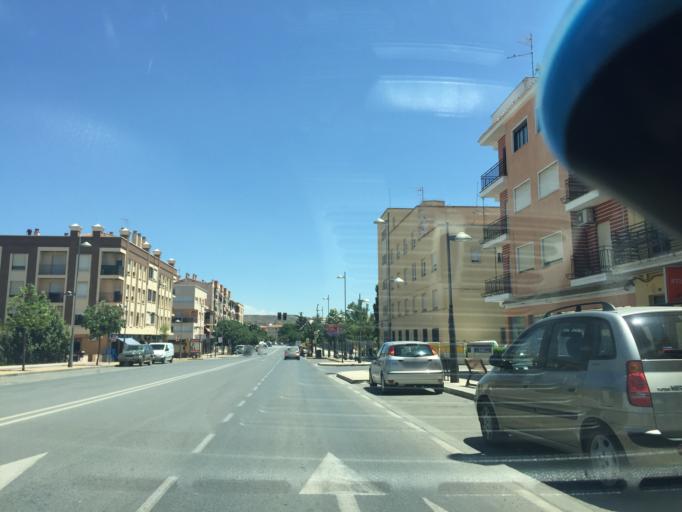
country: ES
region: Andalusia
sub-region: Provincia de Granada
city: Guadix
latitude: 37.3033
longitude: -3.1396
